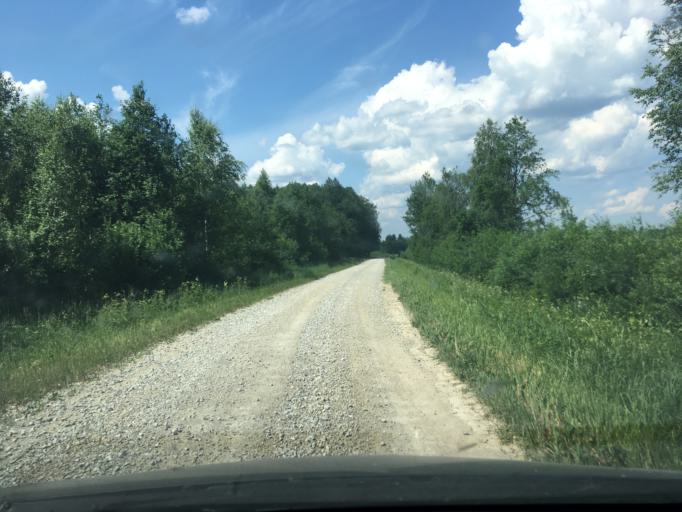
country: EE
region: Raplamaa
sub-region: Maerjamaa vald
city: Marjamaa
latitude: 58.7983
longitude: 24.4537
